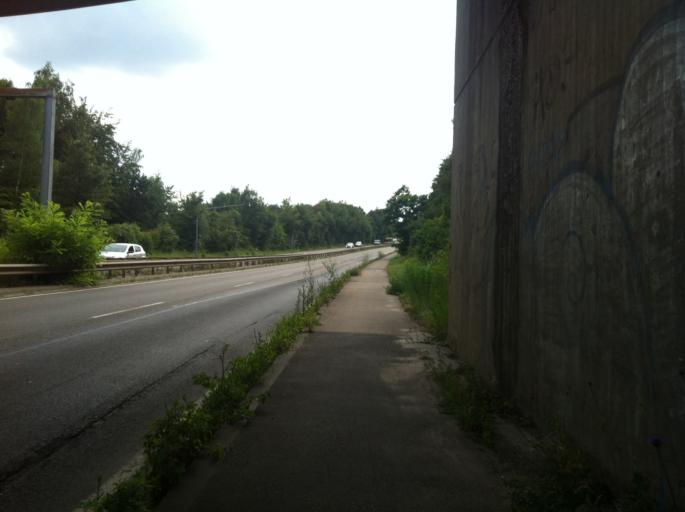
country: DE
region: Rheinland-Pfalz
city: Klein-Winternheim
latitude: 49.9661
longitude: 8.2213
